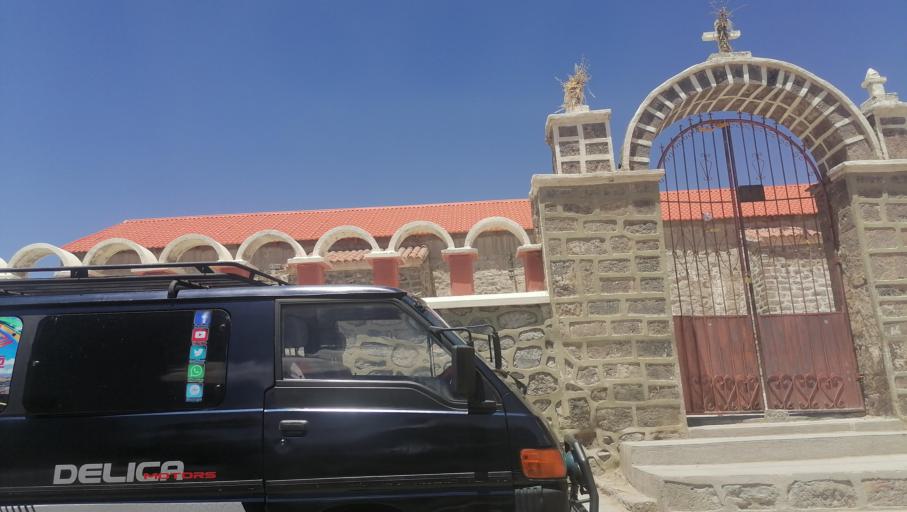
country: BO
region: Oruro
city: Challapata
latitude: -19.1965
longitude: -67.0614
